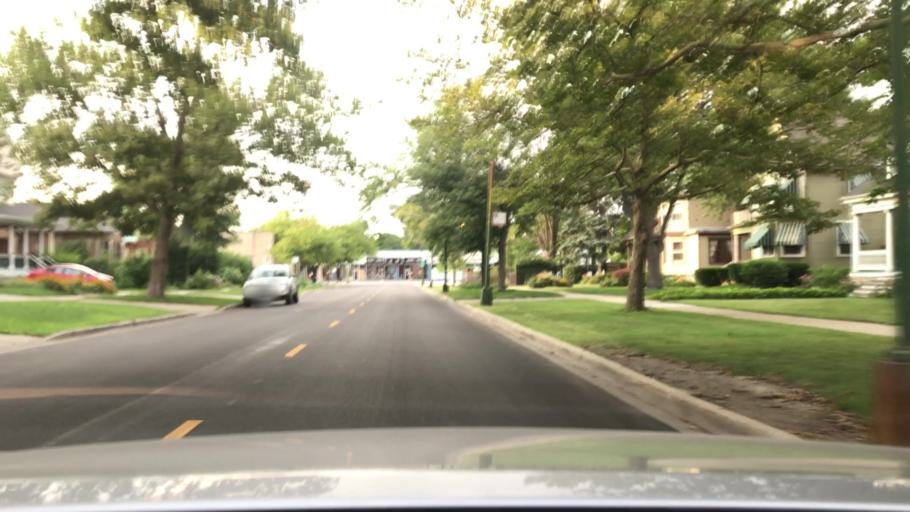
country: US
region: Illinois
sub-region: Cook County
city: Evergreen Park
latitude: 41.7197
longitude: -87.6691
